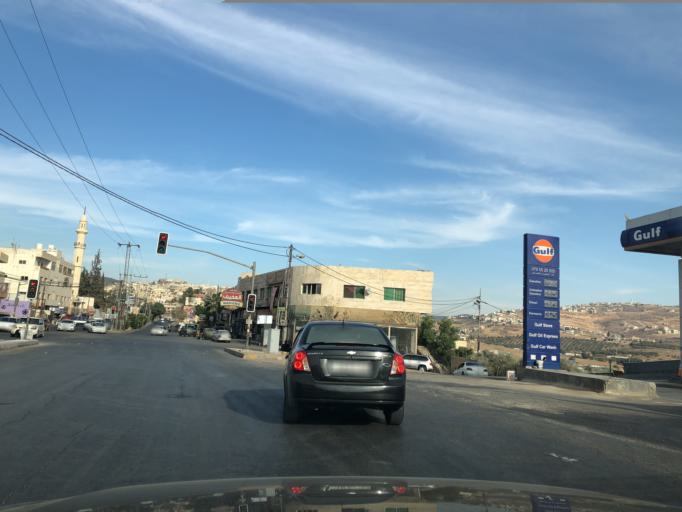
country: JO
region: Jerash
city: Jarash
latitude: 32.2697
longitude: 35.8866
